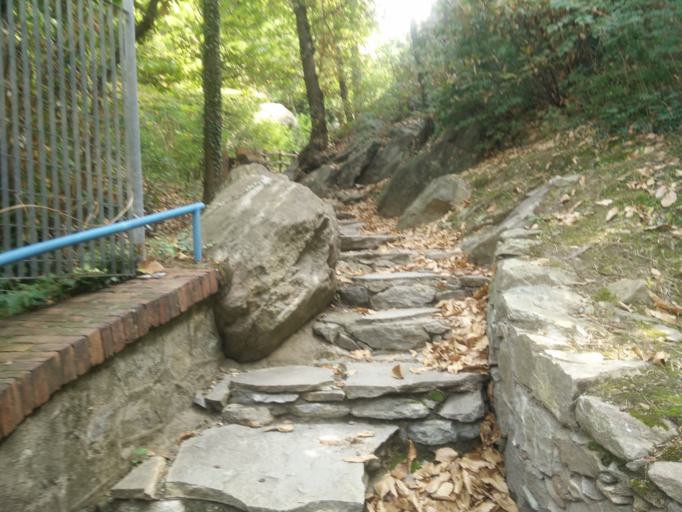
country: IT
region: Aosta Valley
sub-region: Valle d'Aosta
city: Bard
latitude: 45.6062
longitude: 7.7449
